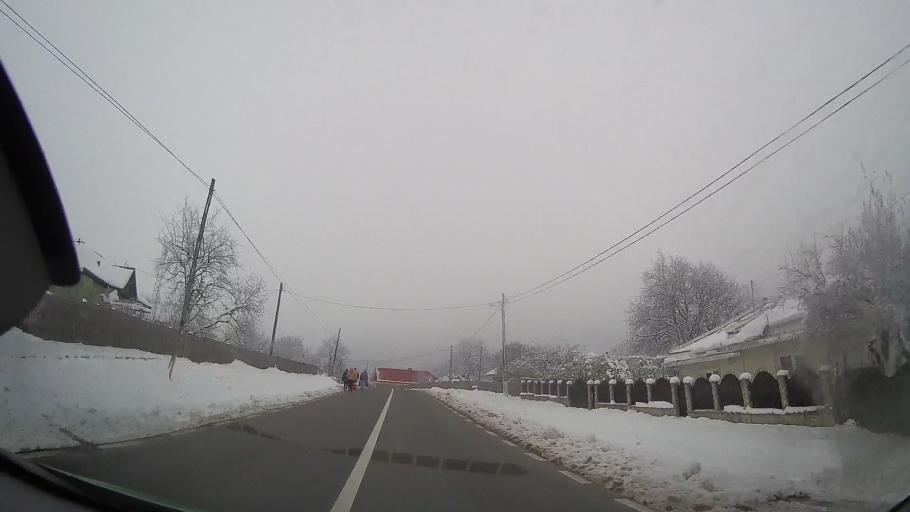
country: RO
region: Neamt
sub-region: Comuna Poenari
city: Poienari
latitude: 46.8797
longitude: 27.1322
